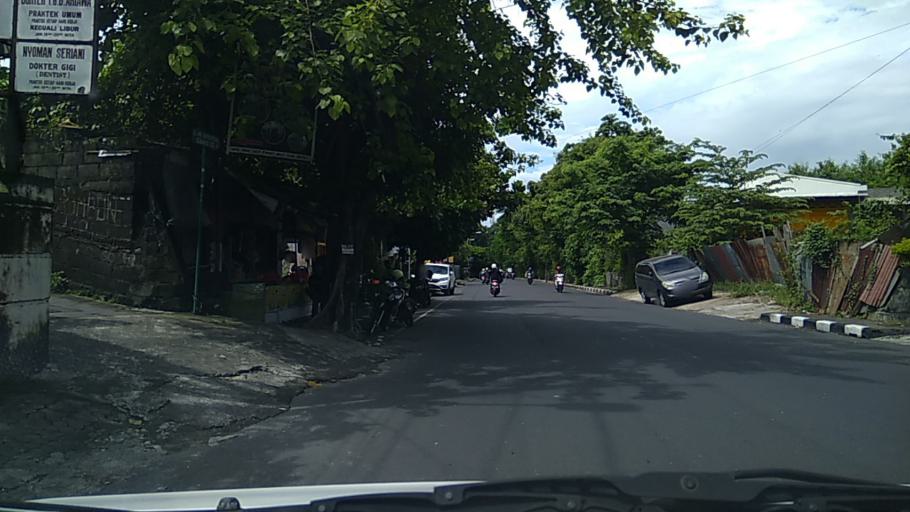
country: ID
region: Bali
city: Dajan Tangluk
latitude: -8.6435
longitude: 115.2491
